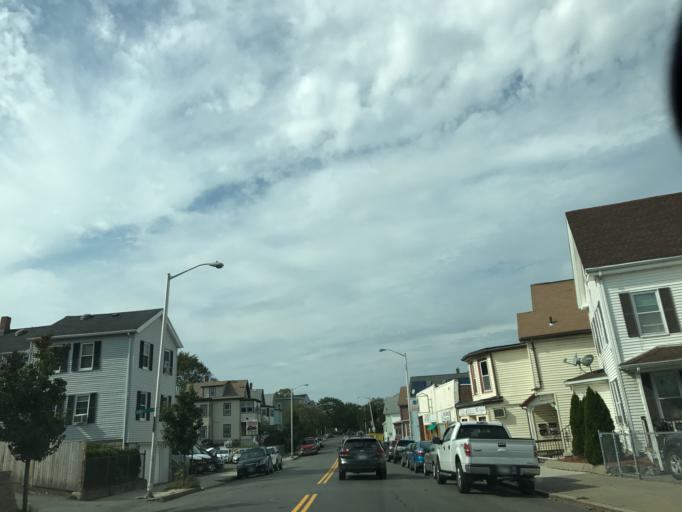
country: US
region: Massachusetts
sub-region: Middlesex County
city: Malden
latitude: 42.4203
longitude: -71.0552
